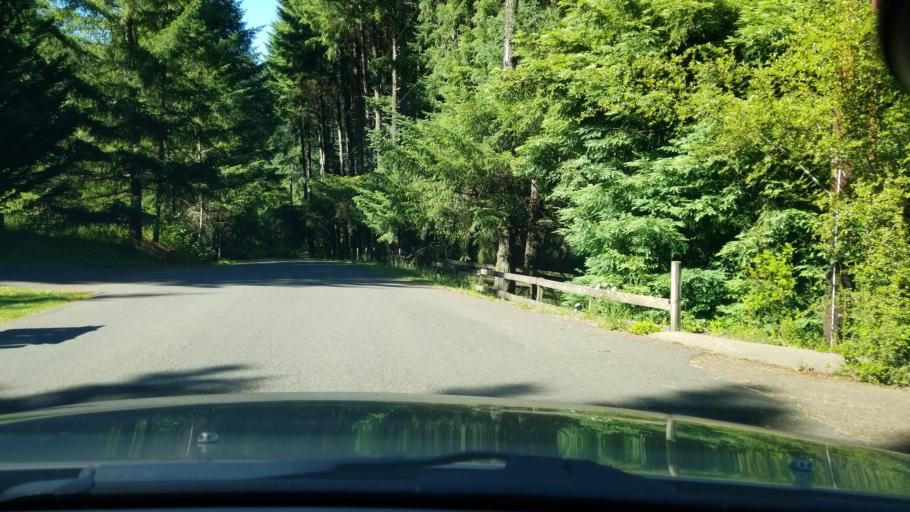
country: US
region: Oregon
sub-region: Yamhill County
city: McMinnville
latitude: 45.2243
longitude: -123.2688
